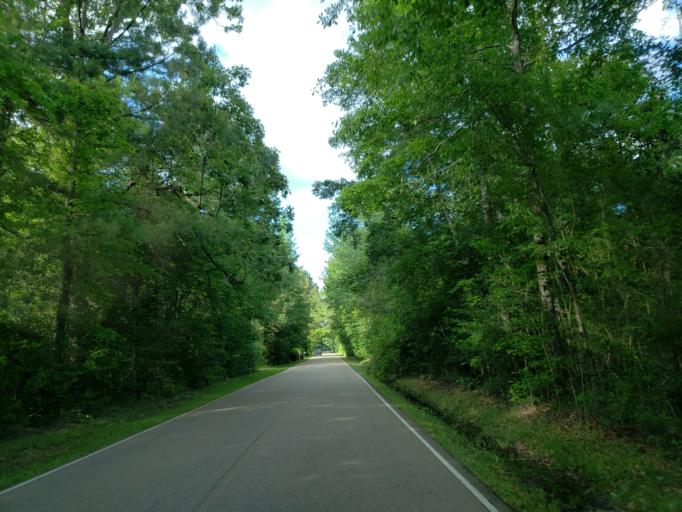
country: US
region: Mississippi
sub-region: Forrest County
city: Hattiesburg
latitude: 31.2539
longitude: -89.2385
